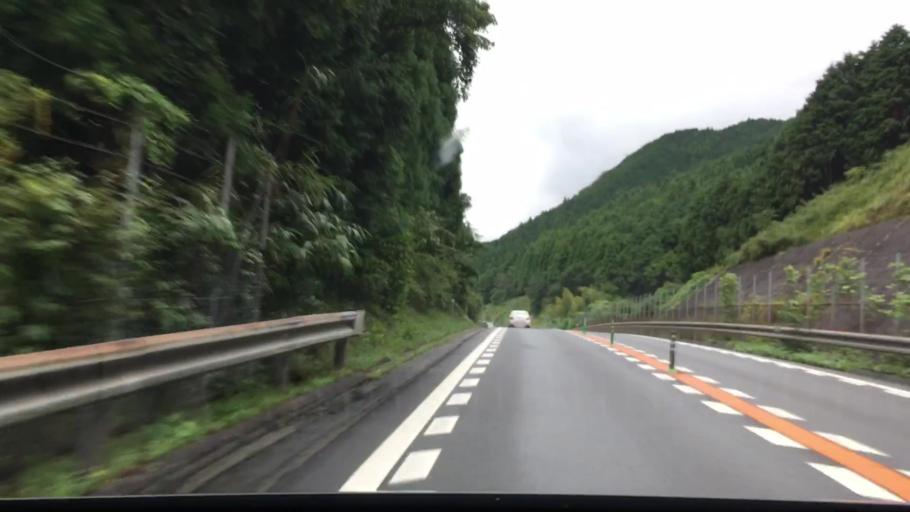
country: JP
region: Hyogo
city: Nishiwaki
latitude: 35.1104
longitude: 134.7812
